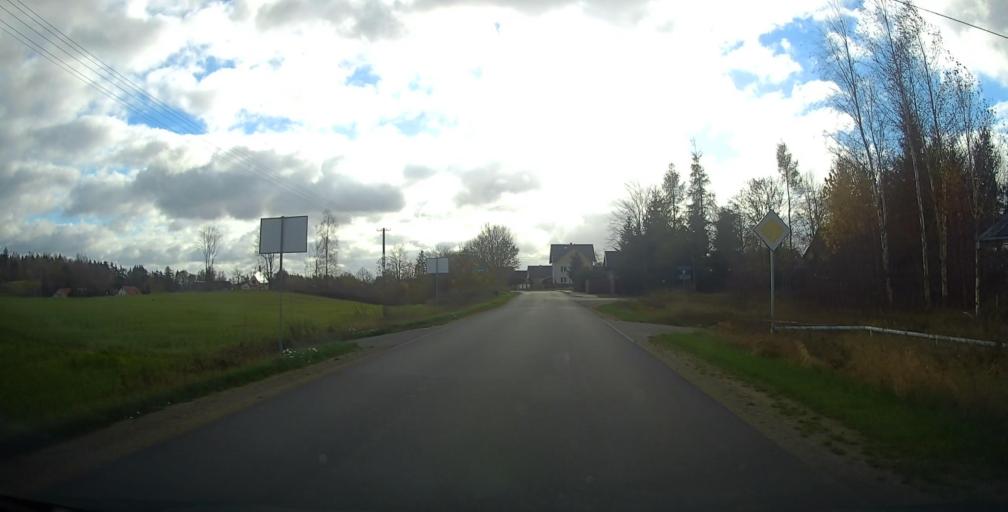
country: PL
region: Podlasie
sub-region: Suwalki
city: Suwalki
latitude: 54.2921
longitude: 22.8789
